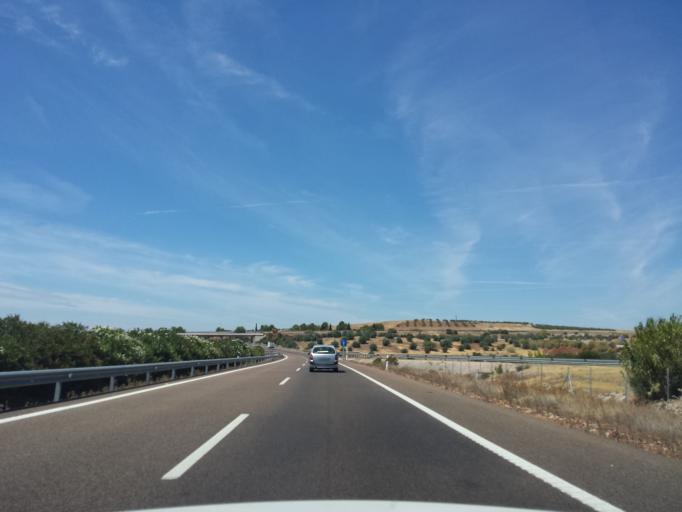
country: ES
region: Extremadura
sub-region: Provincia de Badajoz
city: Merida
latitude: 38.9456
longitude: -6.3336
